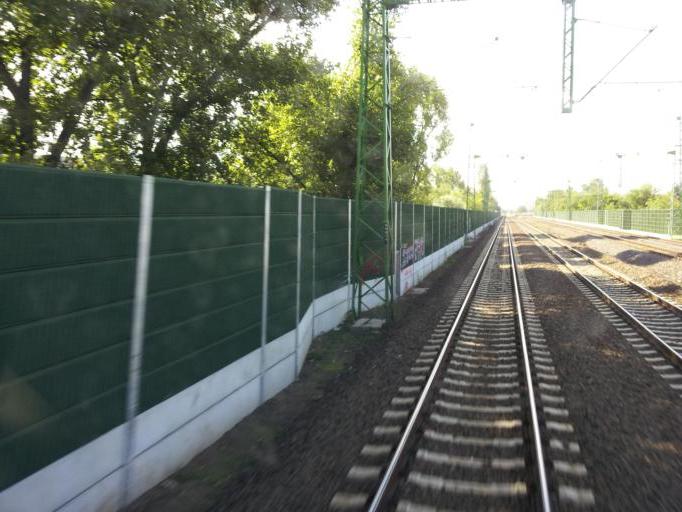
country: HU
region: Budapest
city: Budapest XXII. keruelet
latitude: 47.4473
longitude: 19.0298
